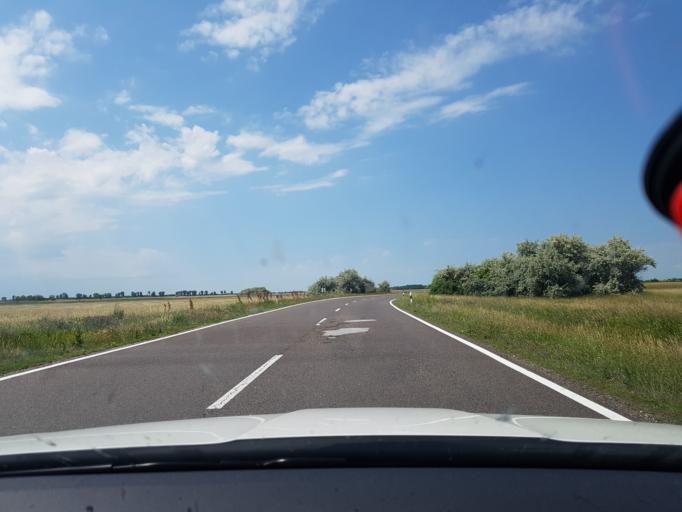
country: HU
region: Hajdu-Bihar
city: Egyek
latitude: 47.5463
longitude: 20.8960
